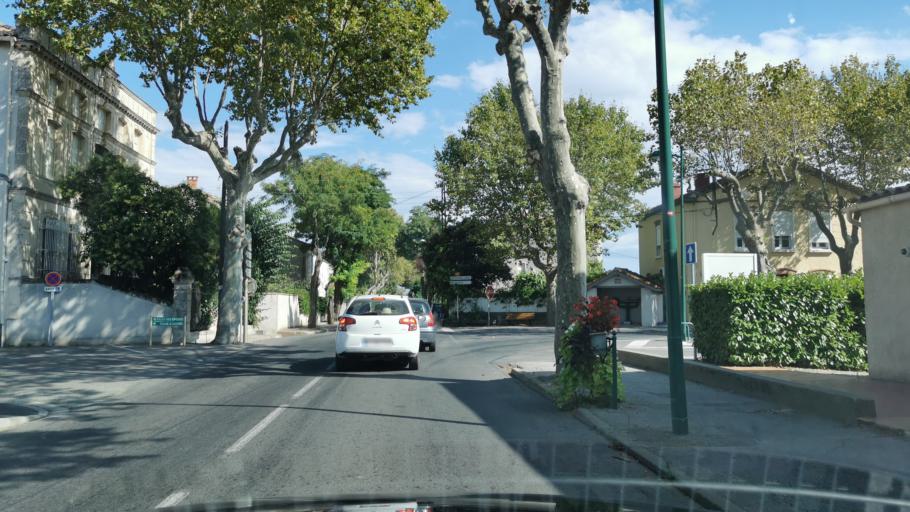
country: FR
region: Languedoc-Roussillon
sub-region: Departement de l'Aude
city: Azille
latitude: 43.2504
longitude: 2.6573
